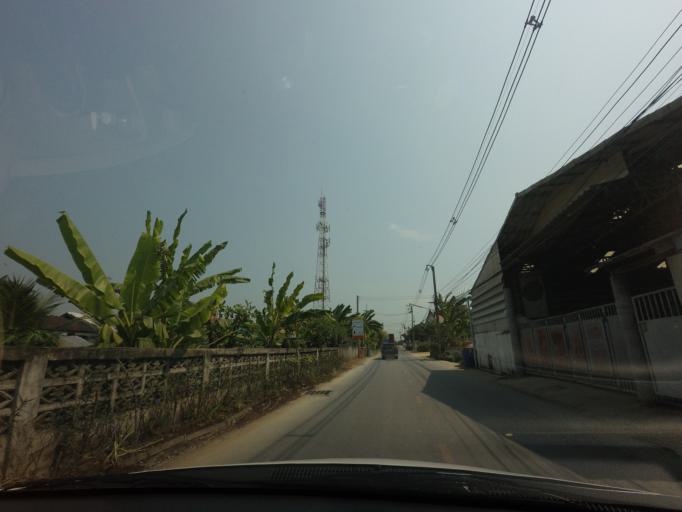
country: TH
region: Nakhon Pathom
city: Sam Phran
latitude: 13.7587
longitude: 100.2478
